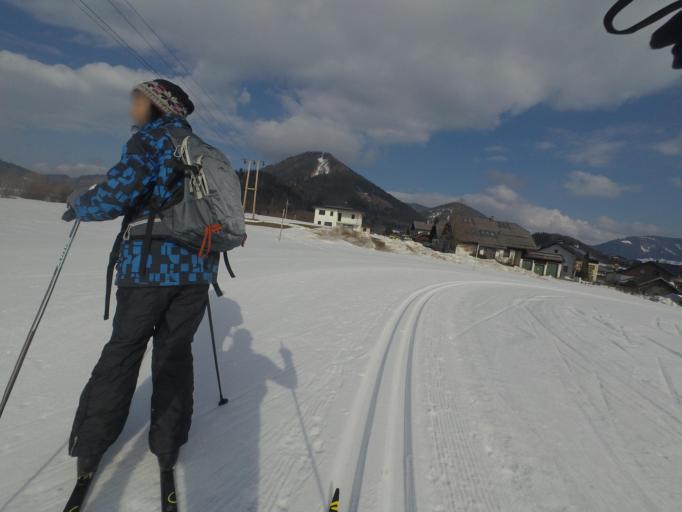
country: AT
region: Salzburg
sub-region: Politischer Bezirk Salzburg-Umgebung
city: Faistenau
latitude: 47.7729
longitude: 13.2396
